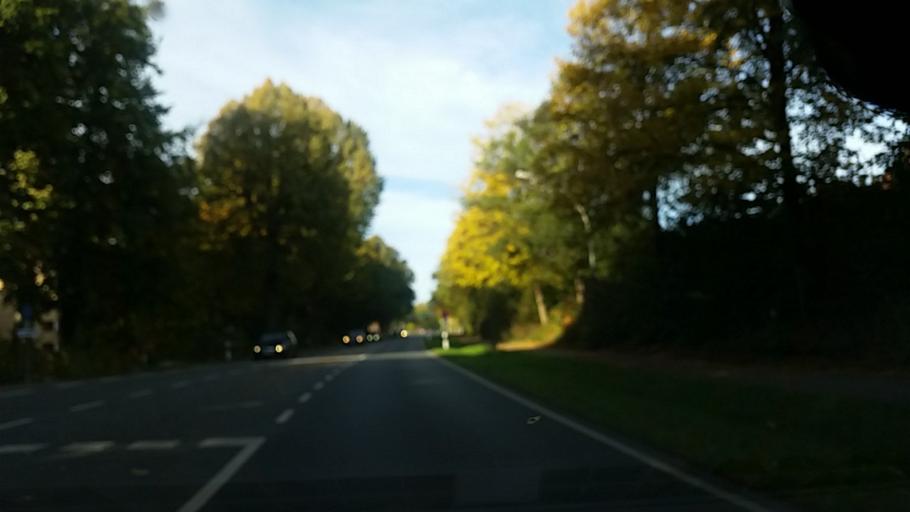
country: DE
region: Schleswig-Holstein
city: Ahrensburg
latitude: 53.6832
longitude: 10.2409
